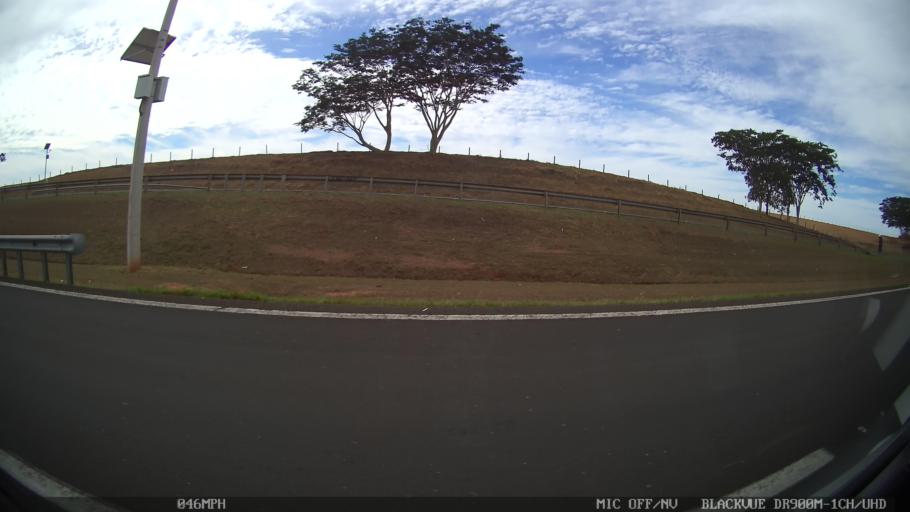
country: BR
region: Sao Paulo
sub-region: Santa Adelia
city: Santa Adelia
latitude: -21.2621
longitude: -48.8761
